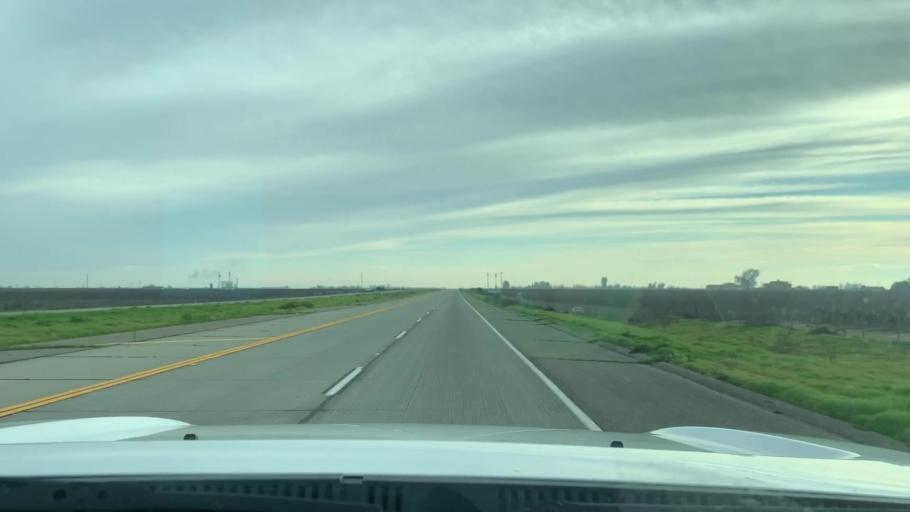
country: US
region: California
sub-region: Fresno County
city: Caruthers
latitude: 36.5733
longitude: -119.7863
